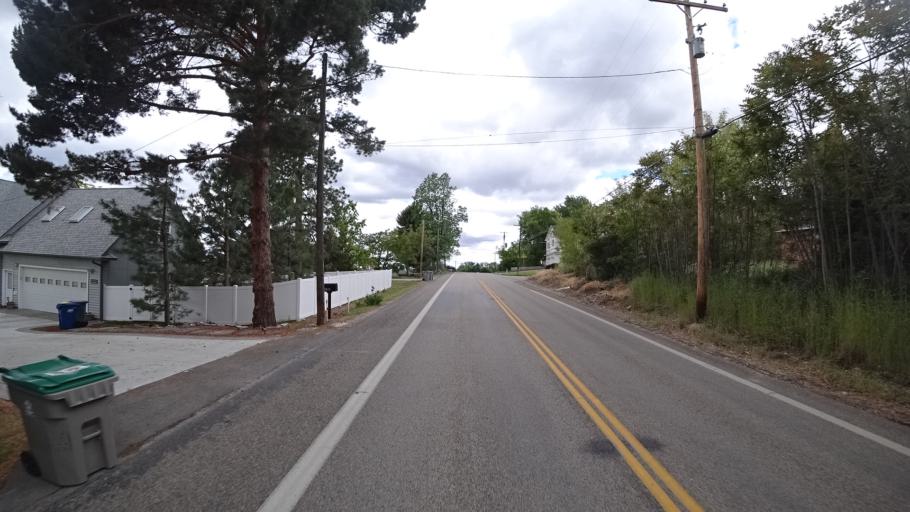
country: US
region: Idaho
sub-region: Ada County
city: Garden City
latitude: 43.6736
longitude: -116.2587
